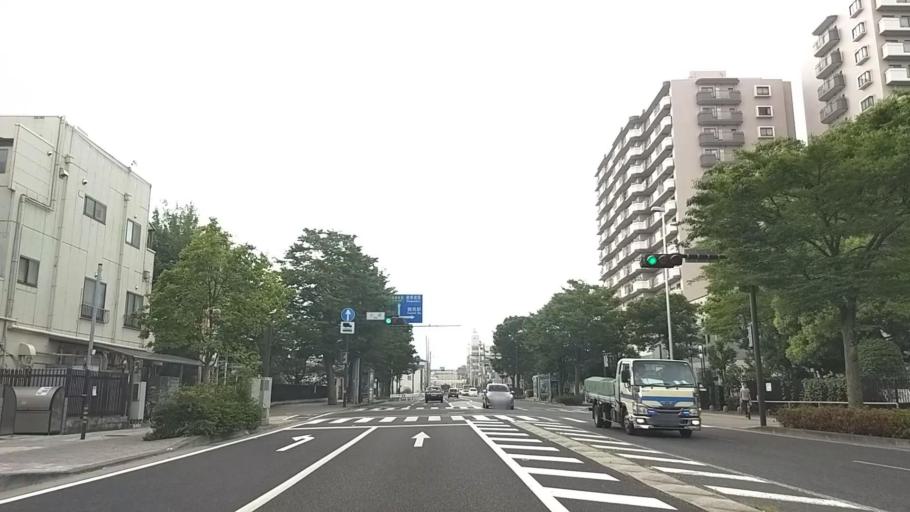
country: JP
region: Kanagawa
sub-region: Kawasaki-shi
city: Kawasaki
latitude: 35.5130
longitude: 139.6971
